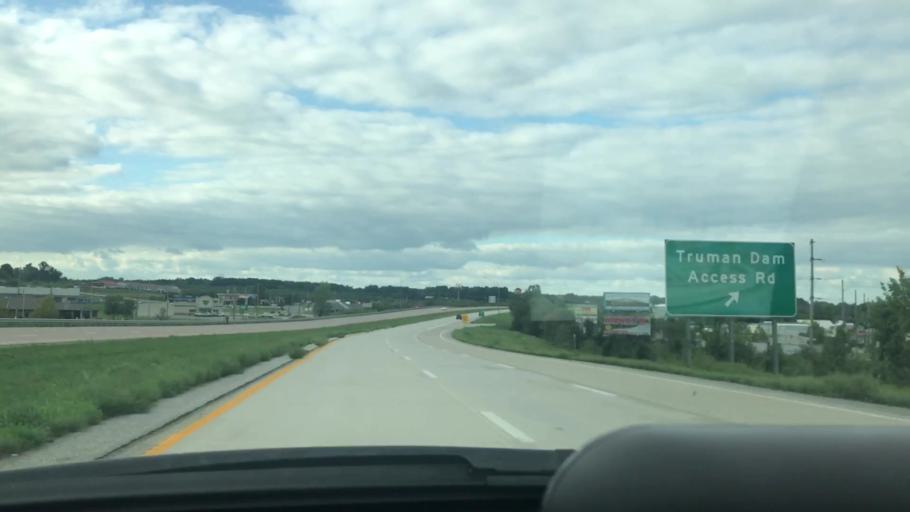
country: US
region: Missouri
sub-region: Benton County
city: Warsaw
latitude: 38.2600
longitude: -93.3661
